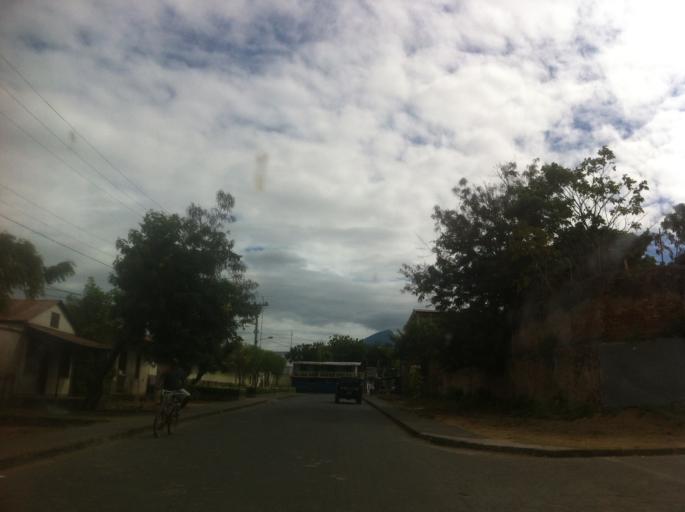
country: NI
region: Granada
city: Granada
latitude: 11.9394
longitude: -85.9524
